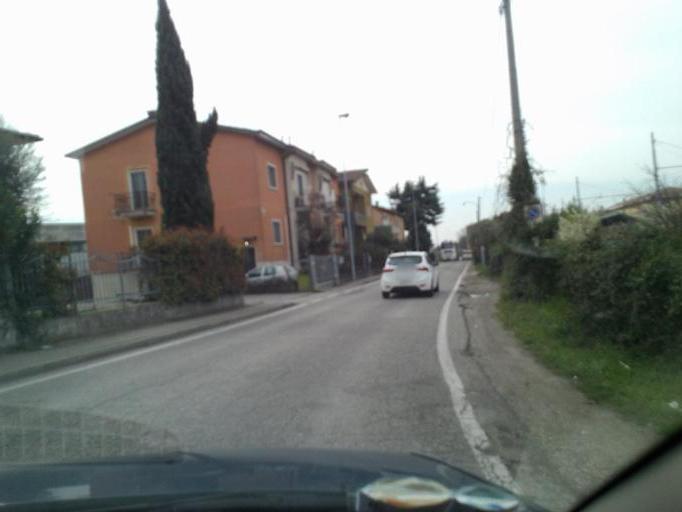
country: IT
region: Veneto
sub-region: Provincia di Verona
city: Villafranca di Verona
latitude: 45.3509
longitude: 10.8503
